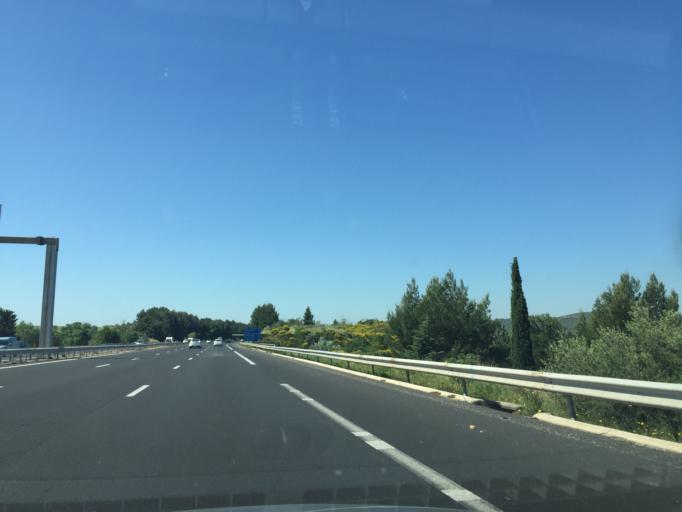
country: FR
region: Languedoc-Roussillon
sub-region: Departement du Gard
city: Remoulins
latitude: 43.9316
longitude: 4.5965
